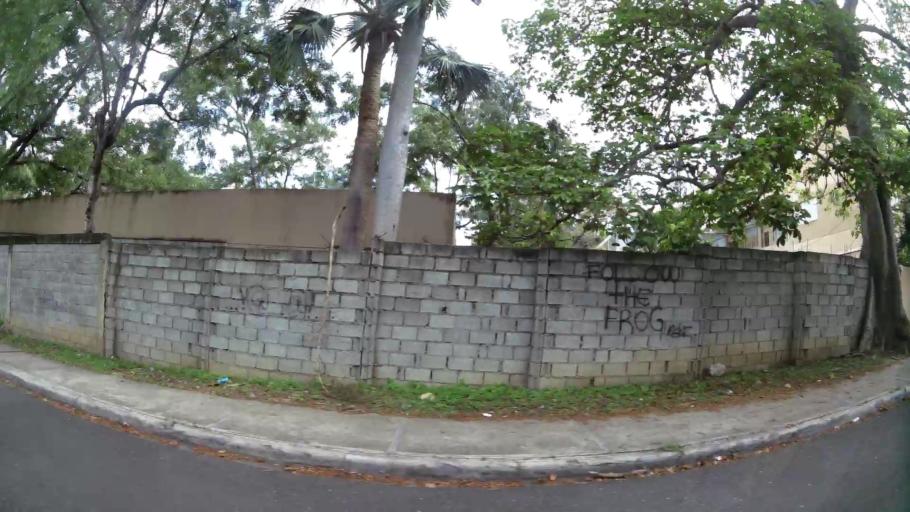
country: DO
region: Santiago
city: Santiago de los Caballeros
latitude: 19.4588
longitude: -70.6892
